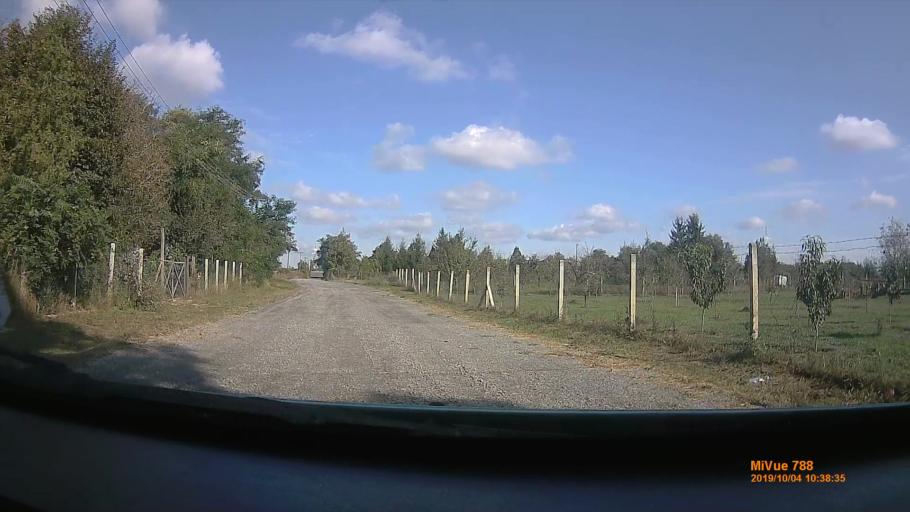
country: HU
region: Szabolcs-Szatmar-Bereg
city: Nyirtelek
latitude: 47.9738
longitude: 21.6632
